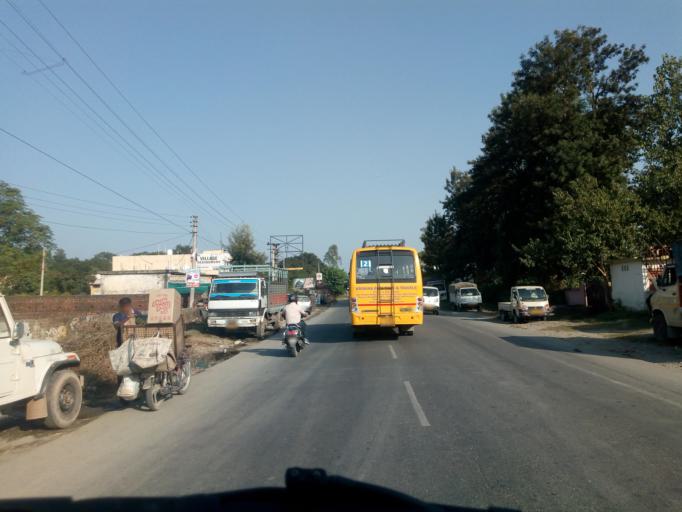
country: IN
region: Uttarakhand
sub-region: Dehradun
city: Dehradun
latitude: 30.3446
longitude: 77.9113
